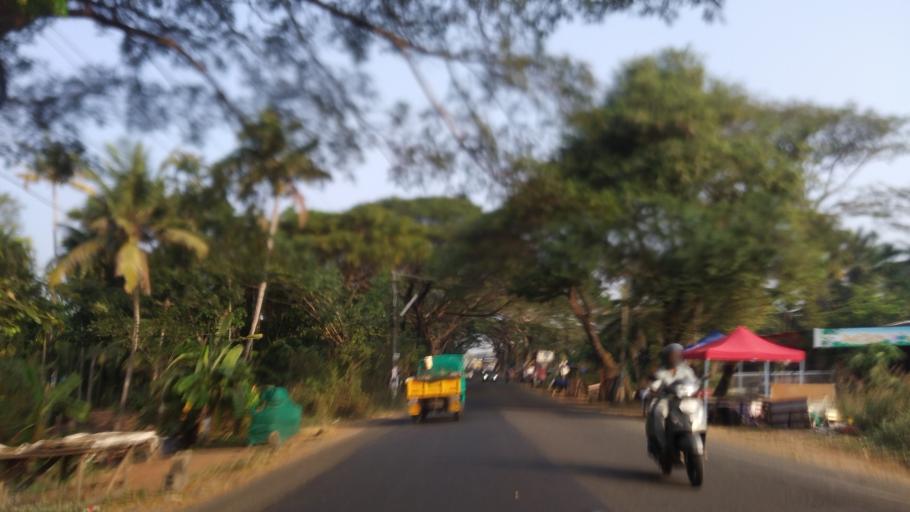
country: IN
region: Kerala
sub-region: Thrissur District
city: Kodungallur
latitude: 10.1962
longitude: 76.2009
